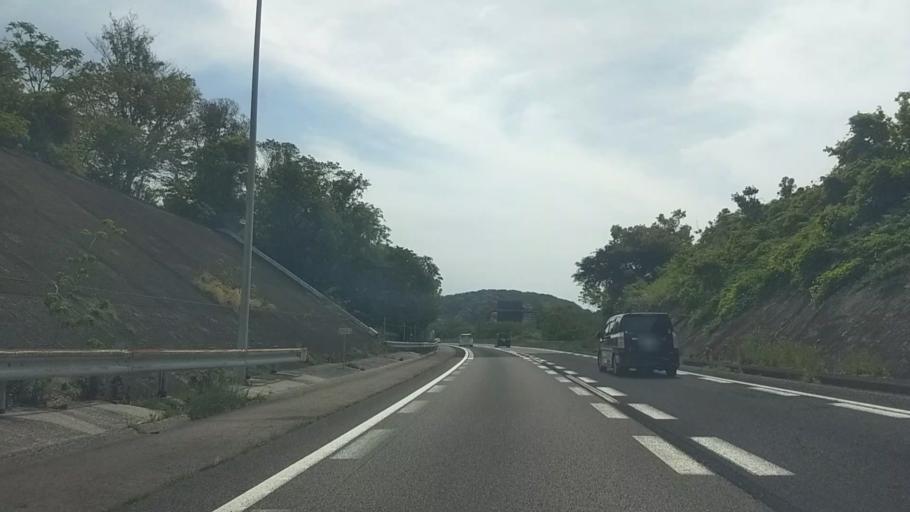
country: JP
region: Shizuoka
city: Kosai-shi
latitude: 34.8093
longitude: 137.5579
